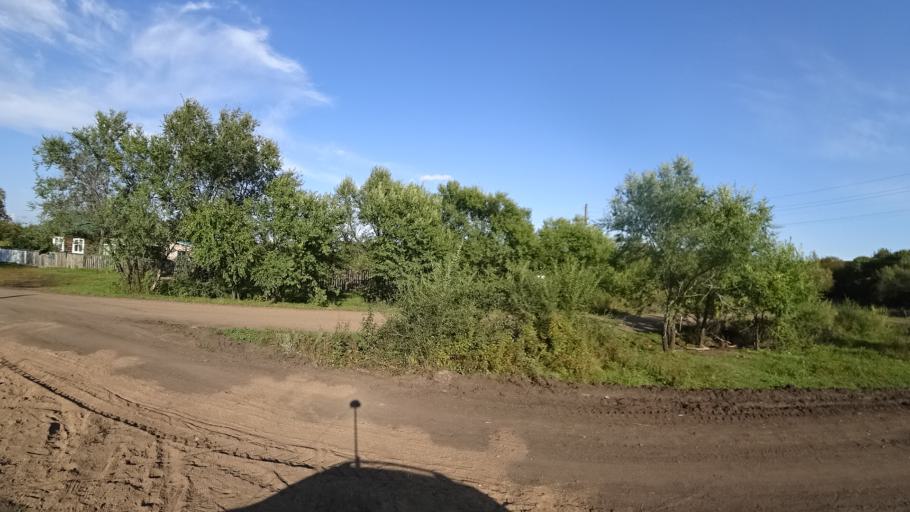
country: RU
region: Amur
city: Arkhara
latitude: 49.3520
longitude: 130.1105
